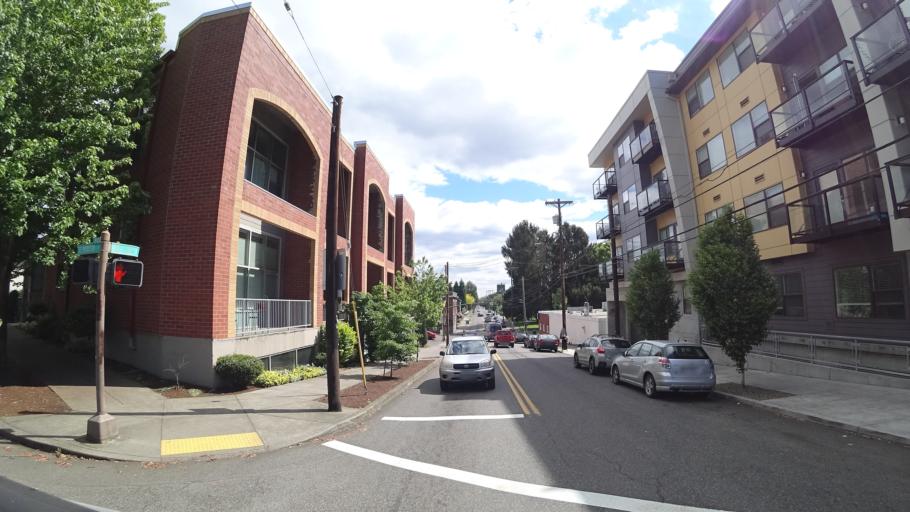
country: US
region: Oregon
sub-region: Multnomah County
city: Portland
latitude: 45.5171
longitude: -122.6455
